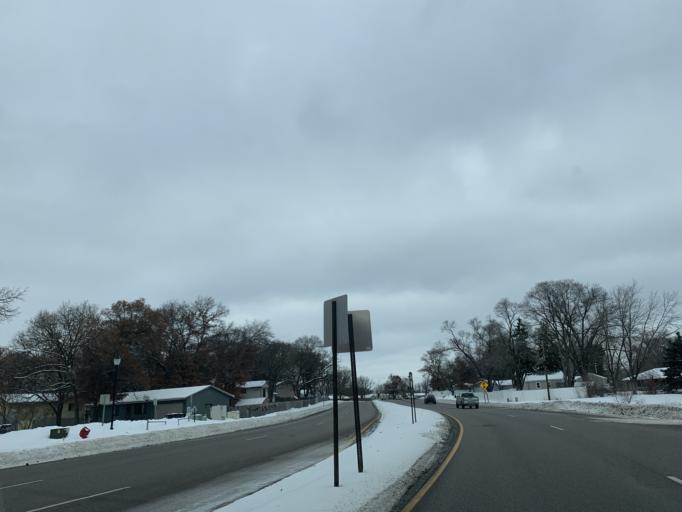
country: US
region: Minnesota
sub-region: Anoka County
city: Blaine
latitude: 45.1616
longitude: -93.2752
